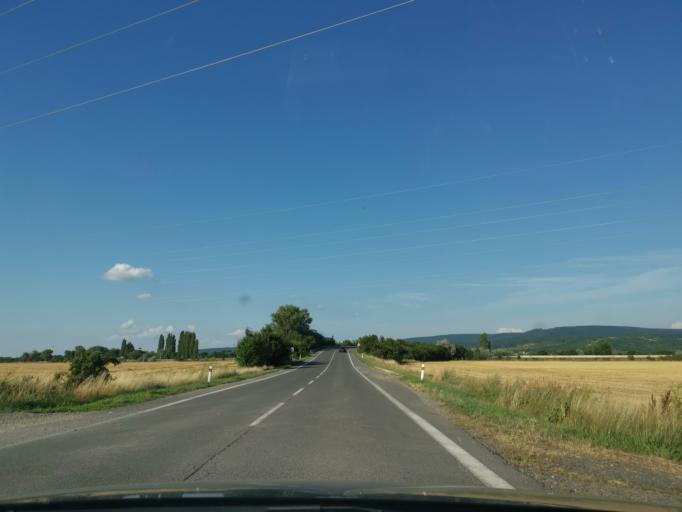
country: SK
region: Bratislavsky
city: Stupava
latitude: 48.2549
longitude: 17.0068
